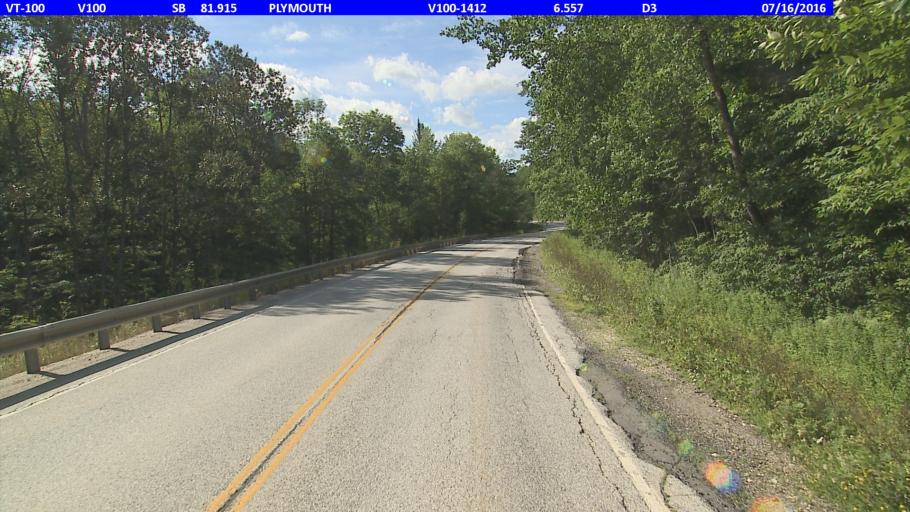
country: US
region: Vermont
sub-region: Rutland County
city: Rutland
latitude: 43.5453
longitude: -72.7507
